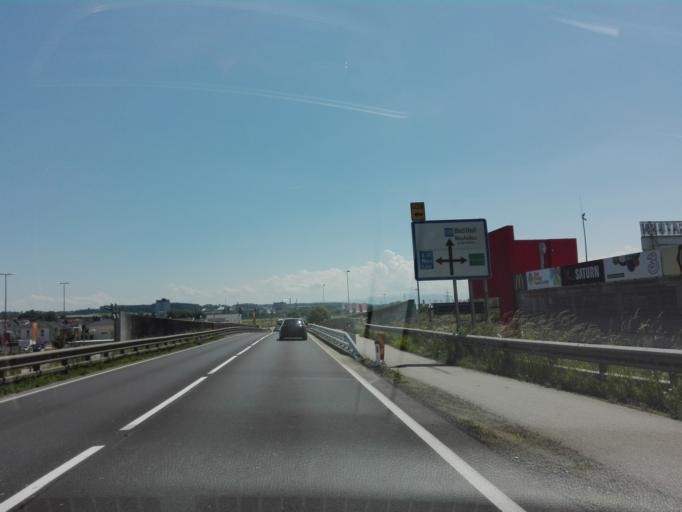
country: AT
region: Upper Austria
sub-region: Politischer Bezirk Linz-Land
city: Traun
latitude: 48.1968
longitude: 14.2489
